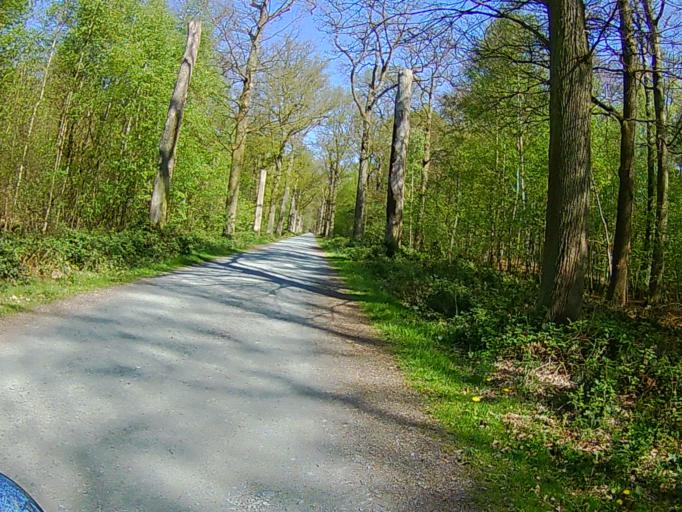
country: BE
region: Flanders
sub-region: Provincie Antwerpen
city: Brasschaat
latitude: 51.2713
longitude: 4.4851
